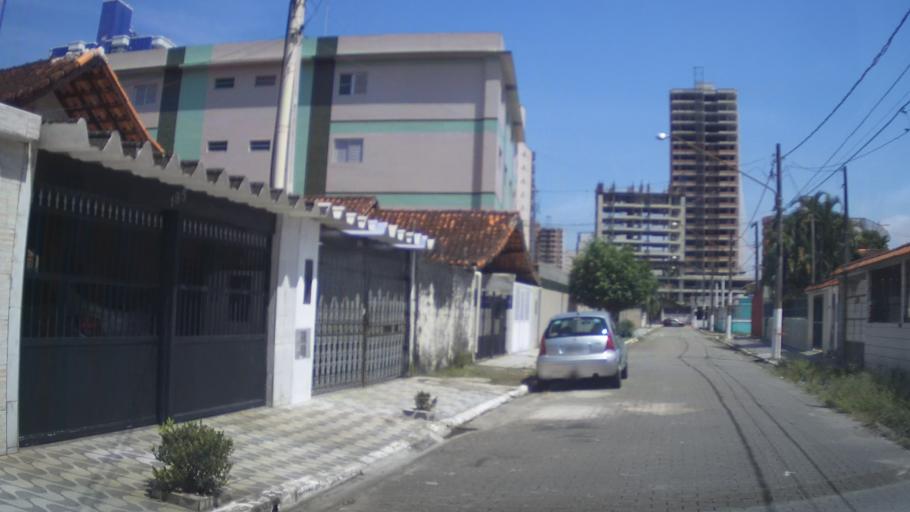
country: BR
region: Sao Paulo
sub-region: Praia Grande
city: Praia Grande
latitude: -24.0160
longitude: -46.4428
